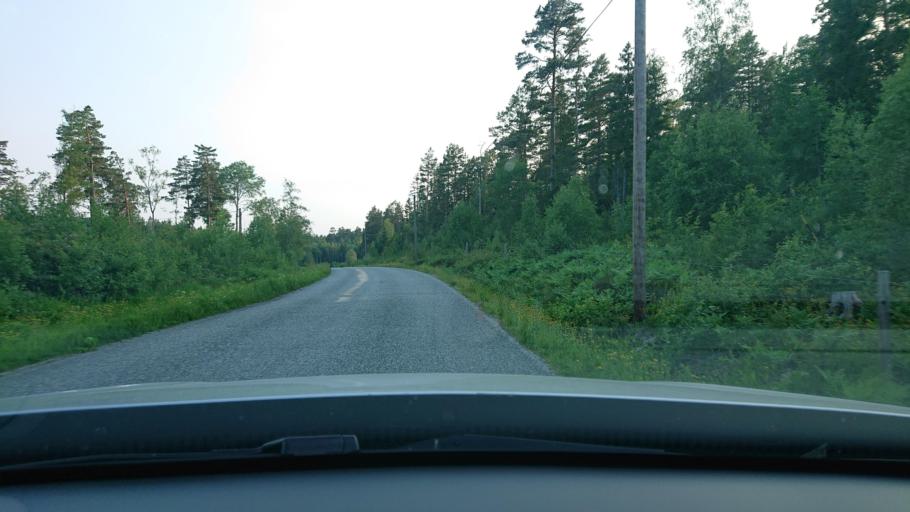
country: SE
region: Stockholm
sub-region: Osterakers Kommun
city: Akersberga
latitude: 59.5165
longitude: 18.3256
